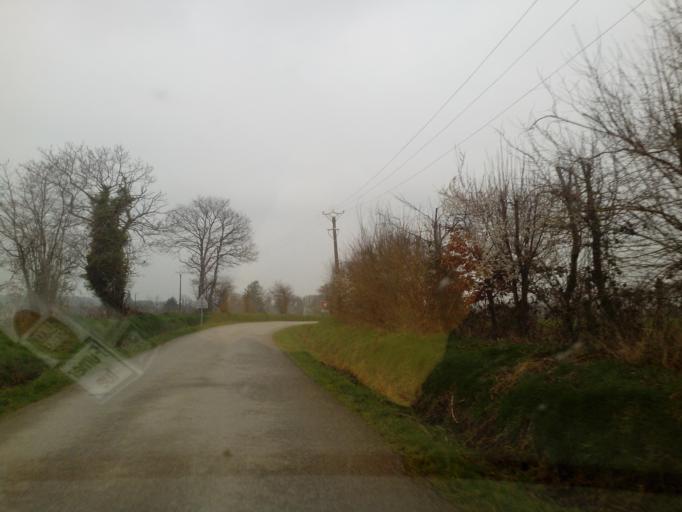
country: FR
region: Brittany
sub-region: Departement du Morbihan
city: Guilliers
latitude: 48.0917
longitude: -2.3698
